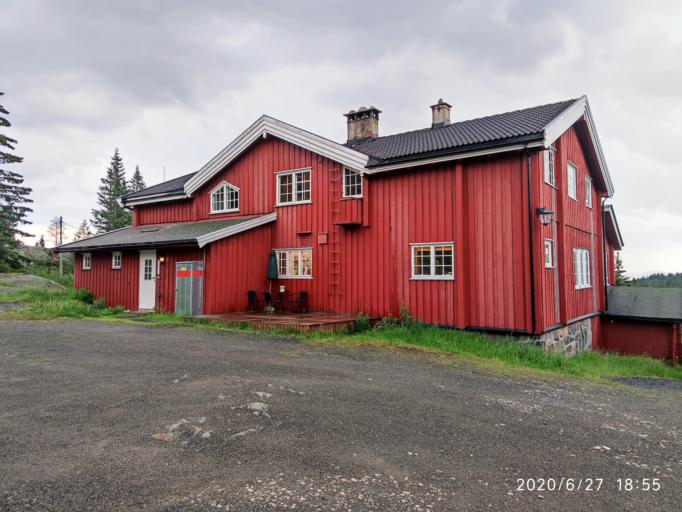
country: NO
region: Buskerud
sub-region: Kongsberg
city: Kongsberg
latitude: 59.6728
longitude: 9.5392
